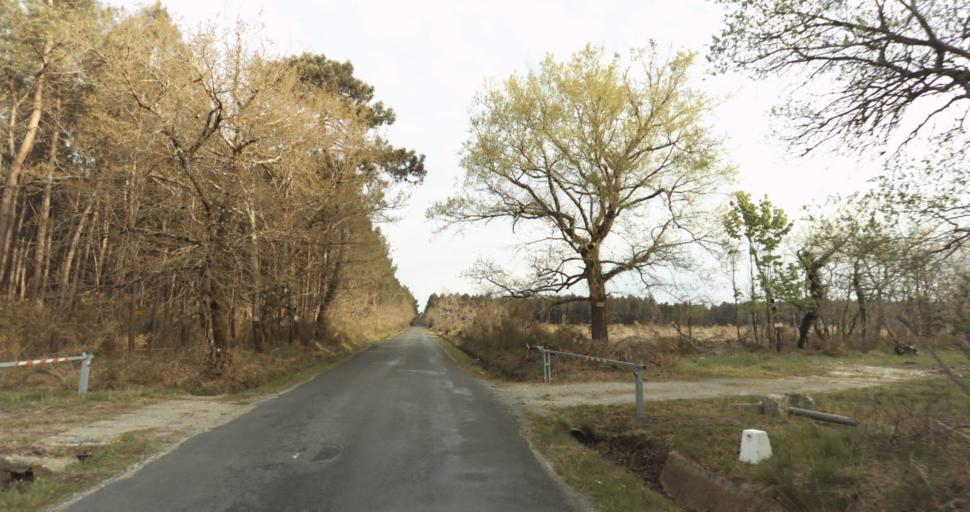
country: FR
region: Aquitaine
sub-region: Departement de la Gironde
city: Martignas-sur-Jalle
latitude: 44.7978
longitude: -0.7642
